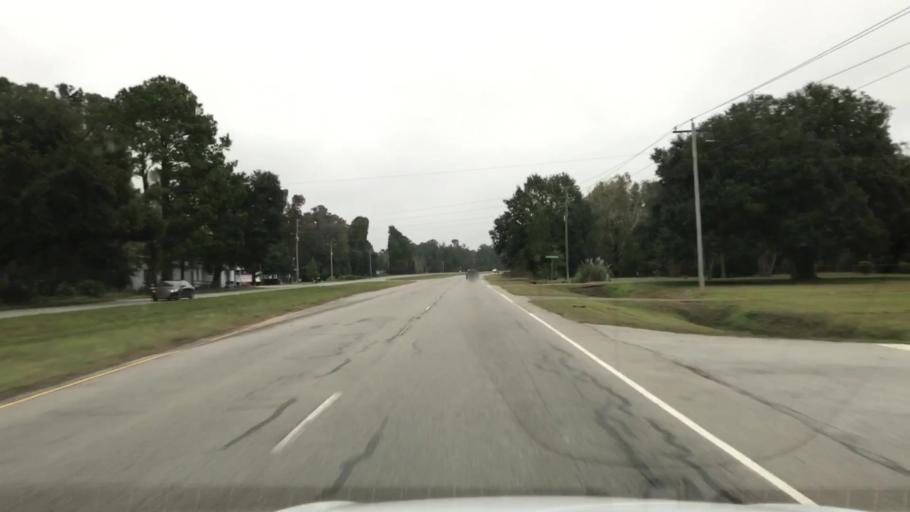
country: US
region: South Carolina
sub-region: Charleston County
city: Awendaw
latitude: 33.0419
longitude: -79.5894
